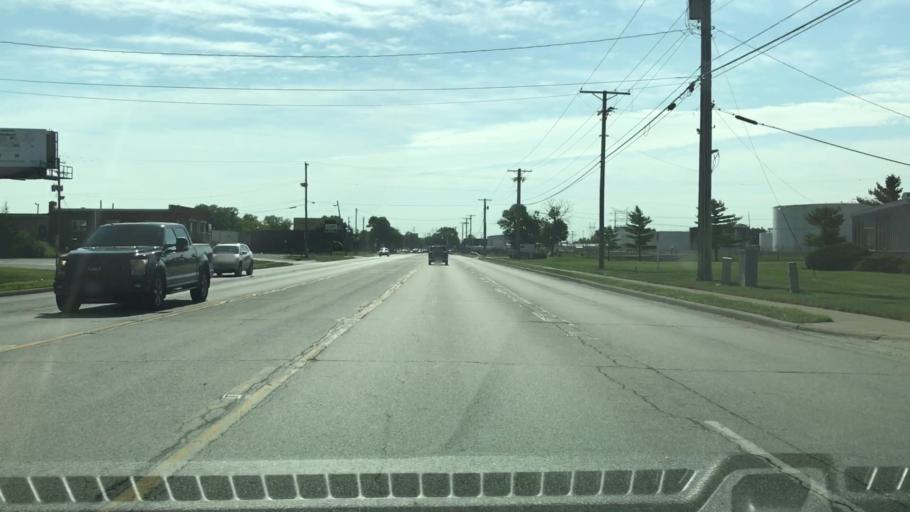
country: US
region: Ohio
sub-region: Franklin County
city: Lincoln Village
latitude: 39.9676
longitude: -83.1018
